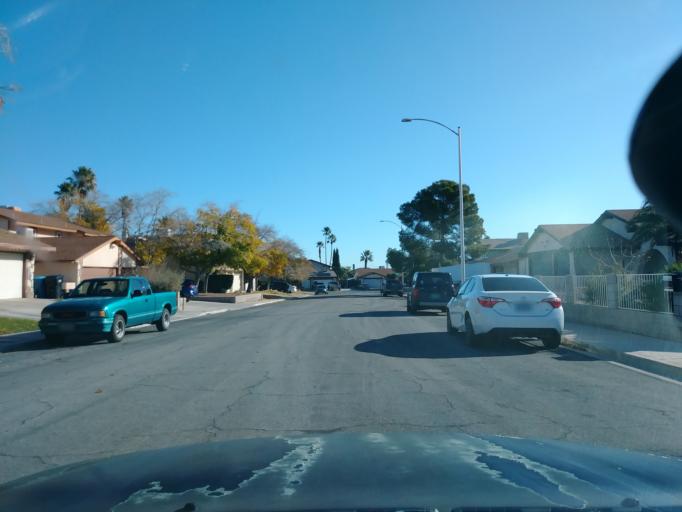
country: US
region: Nevada
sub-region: Clark County
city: Spring Valley
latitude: 36.1486
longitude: -115.2312
